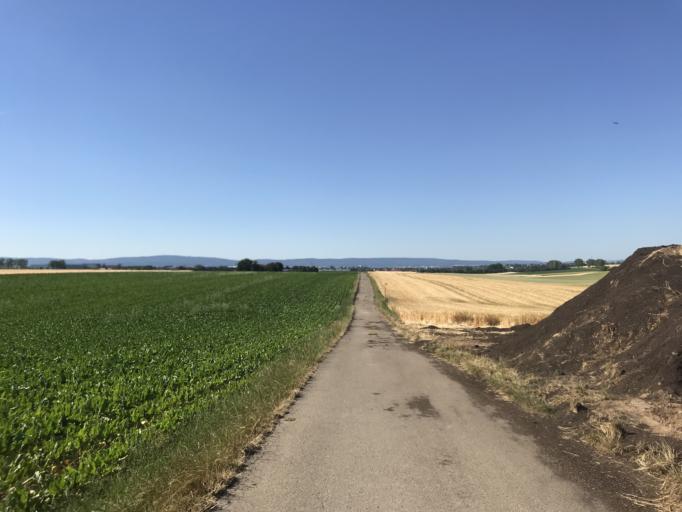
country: DE
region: Rheinland-Pfalz
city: Gau-Bischofsheim
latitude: 49.9325
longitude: 8.2752
